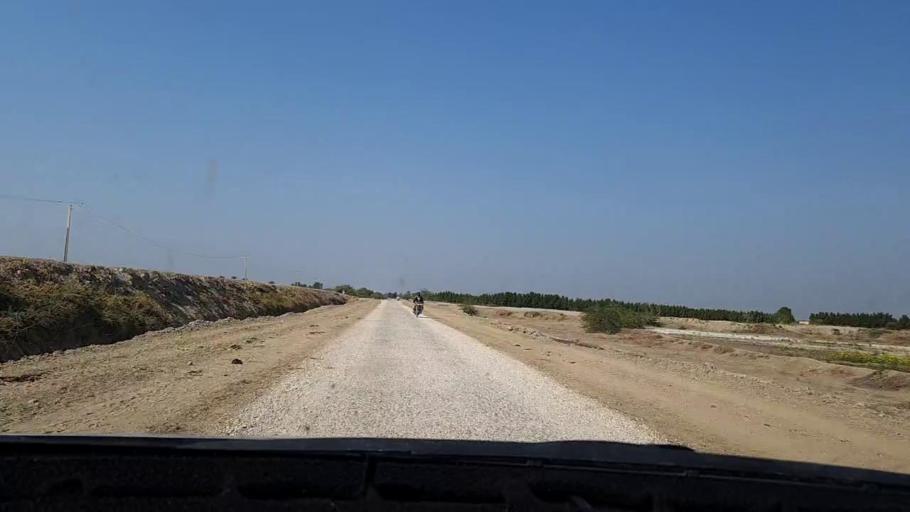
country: PK
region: Sindh
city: Tando Mittha Khan
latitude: 25.8228
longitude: 69.2923
